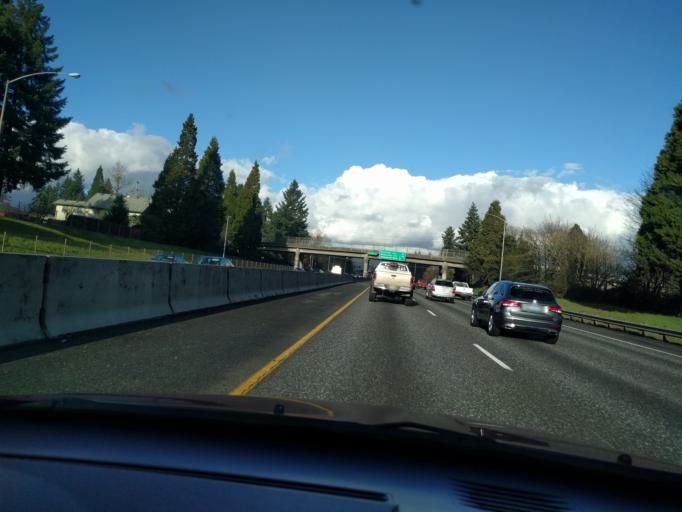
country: US
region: Oregon
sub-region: Clackamas County
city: Clackamas
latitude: 45.3966
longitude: -122.5745
